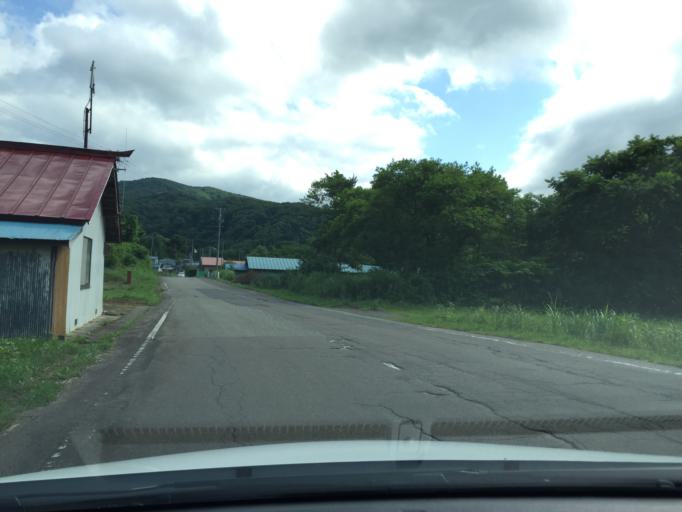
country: JP
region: Fukushima
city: Inawashiro
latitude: 37.2830
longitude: 140.0619
